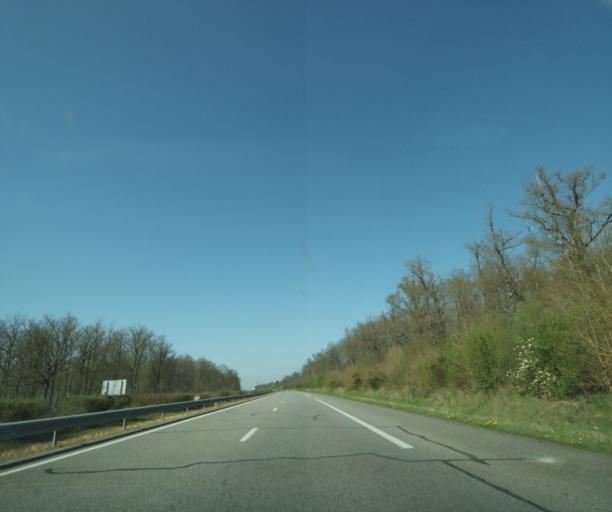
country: FR
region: Centre
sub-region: Departement du Loiret
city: Briare
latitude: 47.7096
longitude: 2.7410
